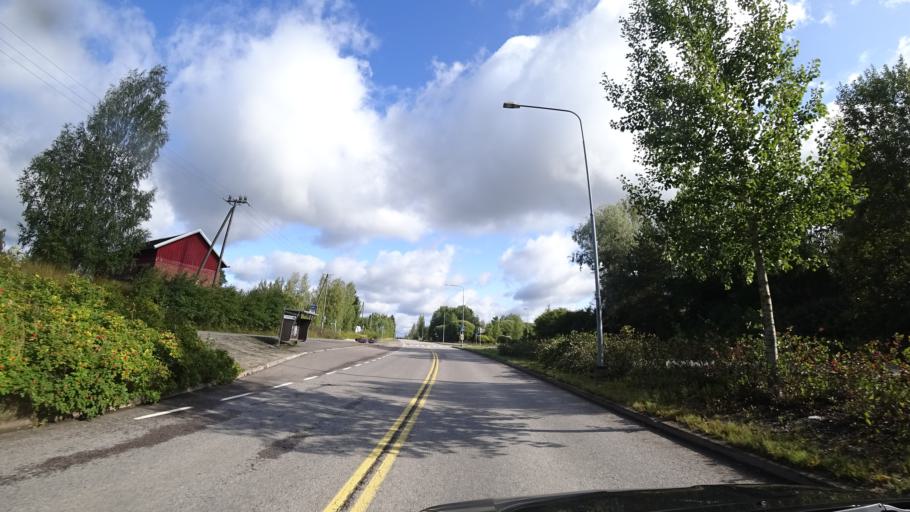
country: FI
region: Uusimaa
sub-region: Helsinki
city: Hyvinge
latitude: 60.5550
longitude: 24.9680
